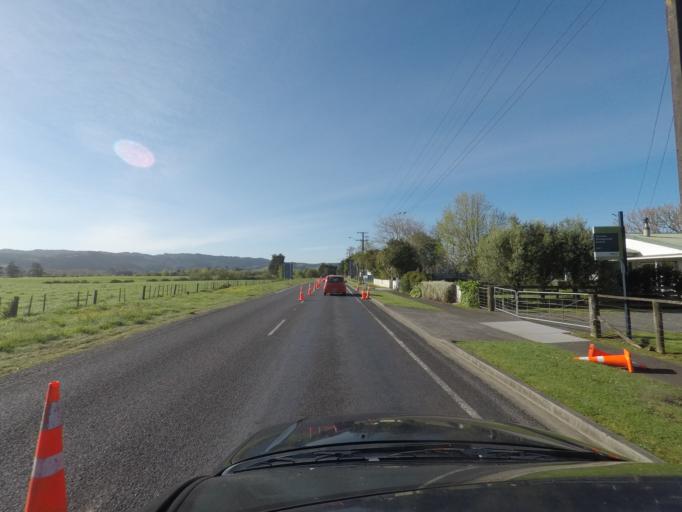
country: NZ
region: Auckland
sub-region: Auckland
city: Red Hill
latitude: -36.9996
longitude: 175.0394
